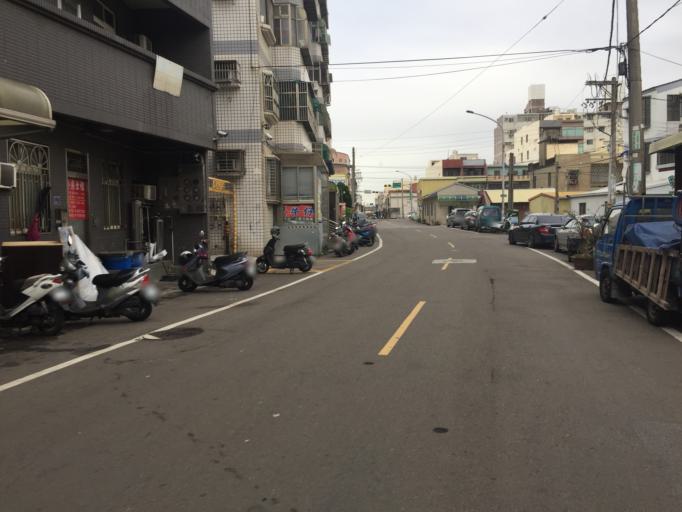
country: TW
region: Taiwan
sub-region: Hsinchu
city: Hsinchu
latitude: 24.7921
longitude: 120.9226
